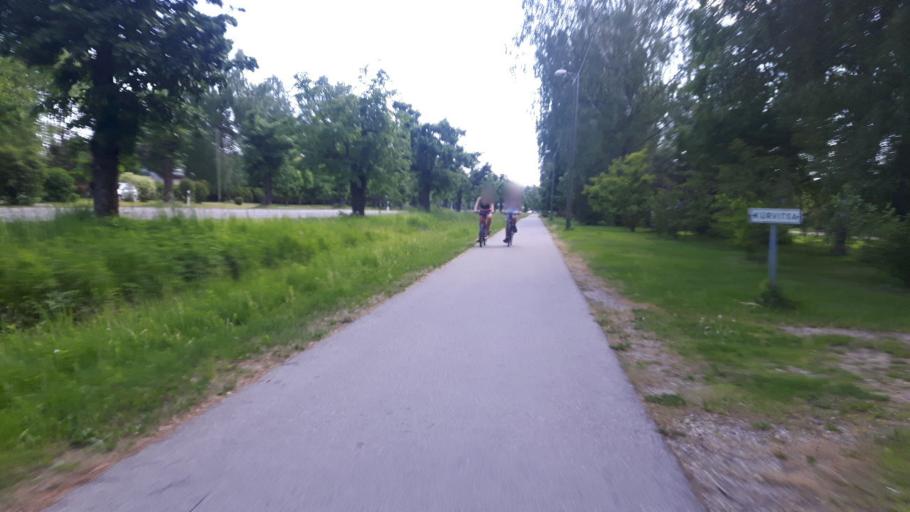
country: EE
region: Paernumaa
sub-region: Paikuse vald
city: Paikuse
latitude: 58.3779
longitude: 24.6261
